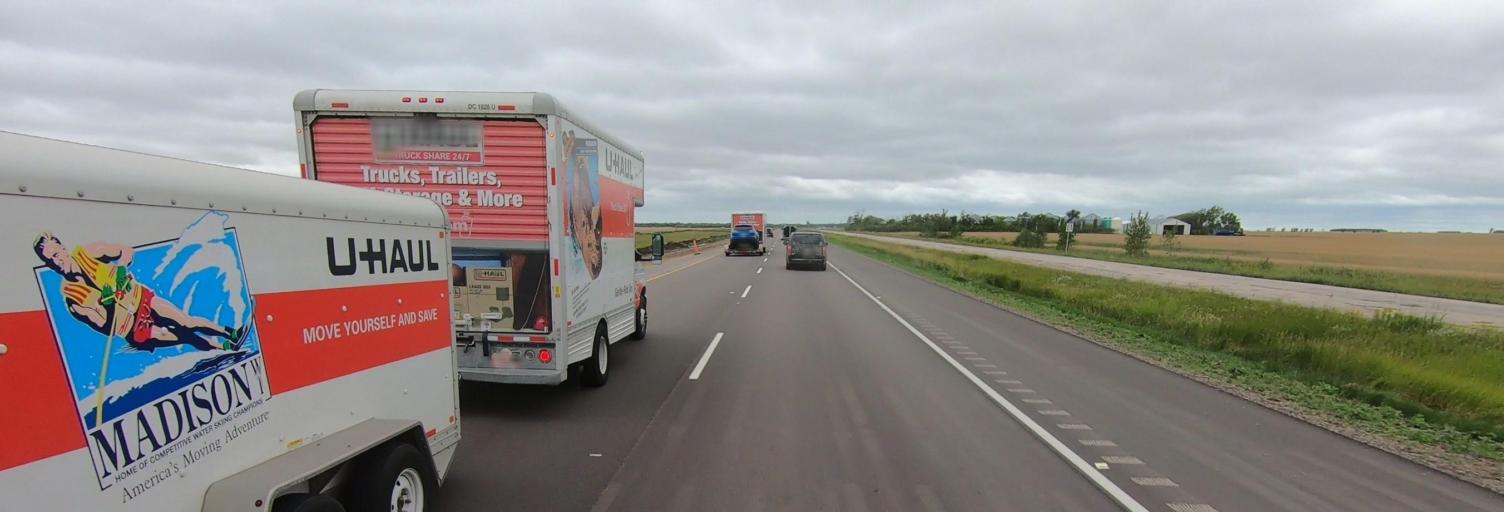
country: CA
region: Manitoba
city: Headingley
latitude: 49.8804
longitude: -97.4495
